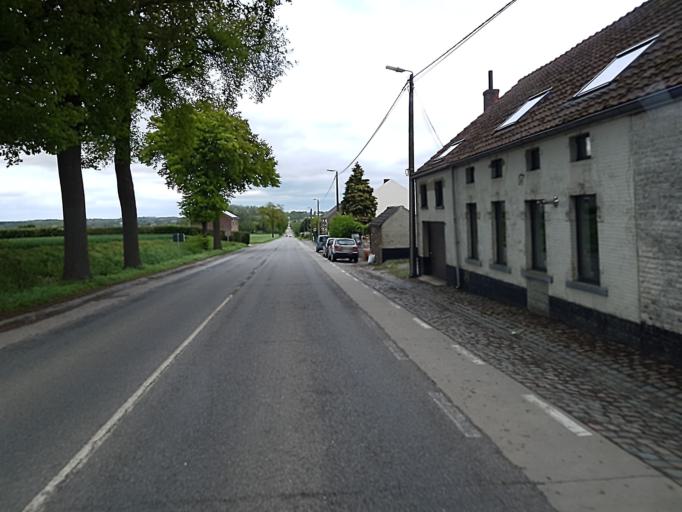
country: BE
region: Wallonia
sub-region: Province du Brabant Wallon
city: Incourt
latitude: 50.6833
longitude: 4.8353
